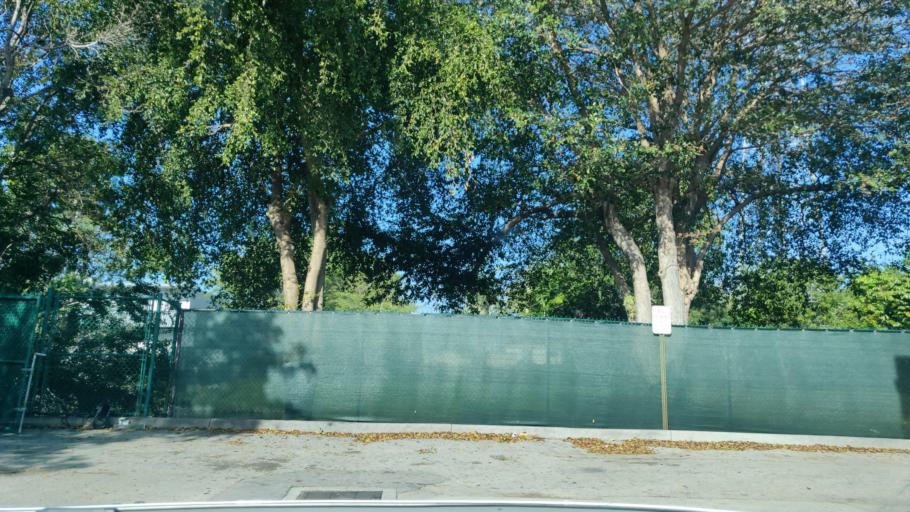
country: US
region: Florida
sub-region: Broward County
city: Tamarac
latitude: 26.1846
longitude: -80.2888
